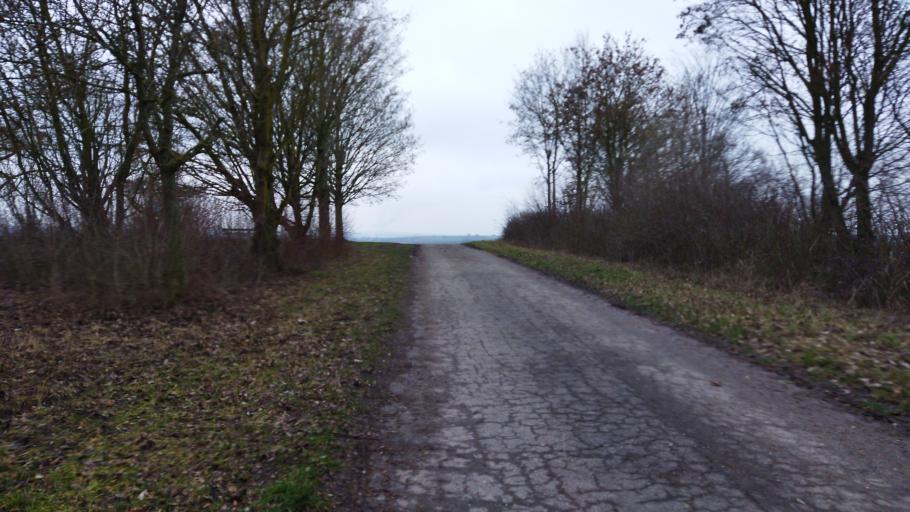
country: DE
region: Baden-Wuerttemberg
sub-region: Regierungsbezirk Stuttgart
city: Nordheim
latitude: 49.1166
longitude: 9.1464
